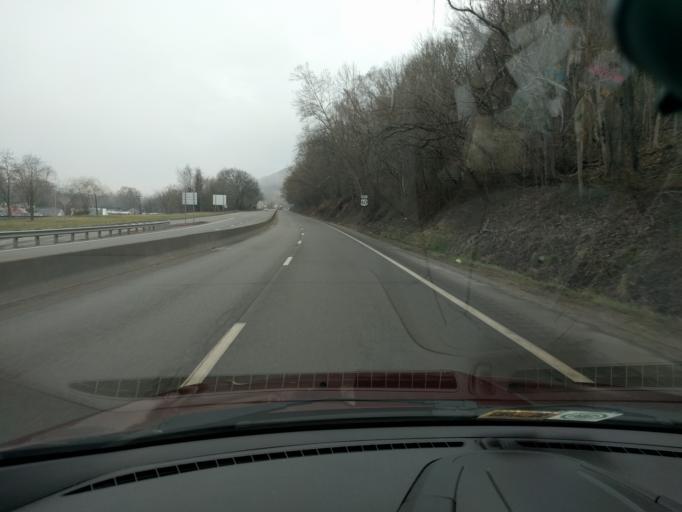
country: US
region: West Virginia
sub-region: Kanawha County
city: Rand
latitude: 38.3011
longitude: -81.5559
